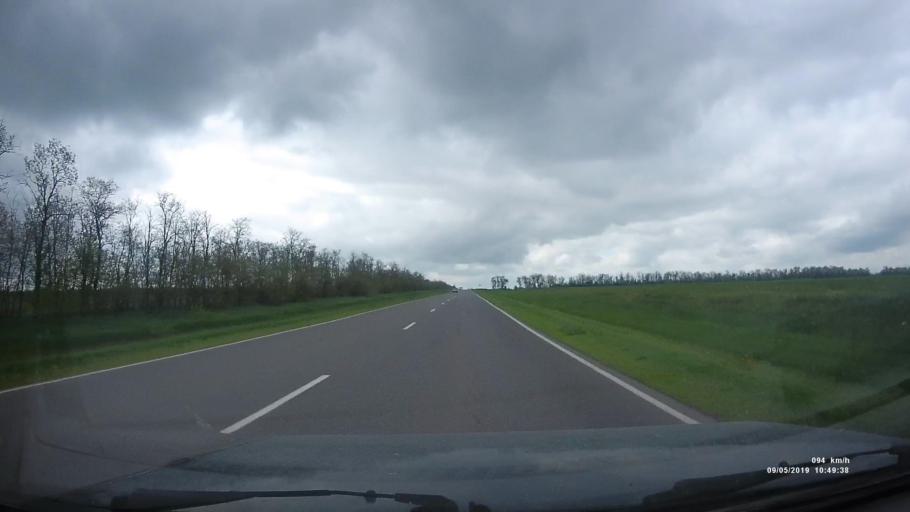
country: RU
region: Rostov
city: Peshkovo
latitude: 46.9396
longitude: 39.3554
